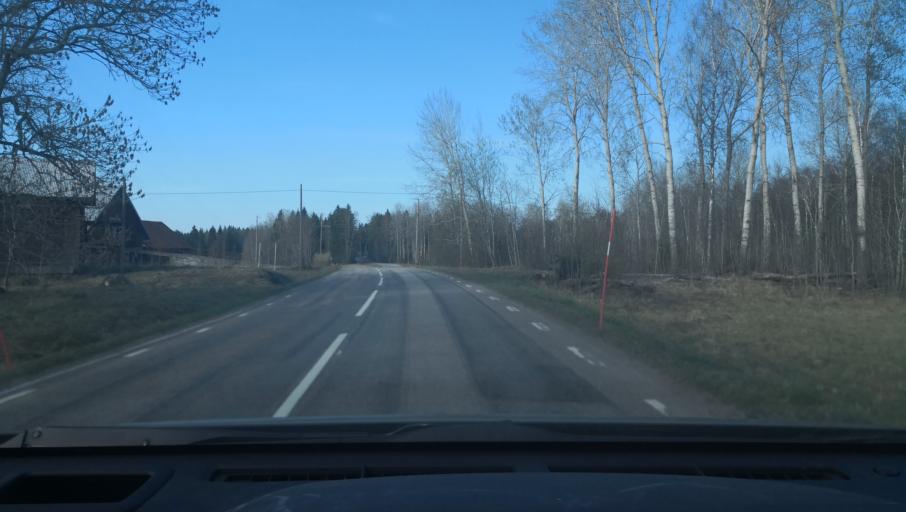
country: SE
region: Uppsala
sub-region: Heby Kommun
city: Heby
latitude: 59.9776
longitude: 16.9049
